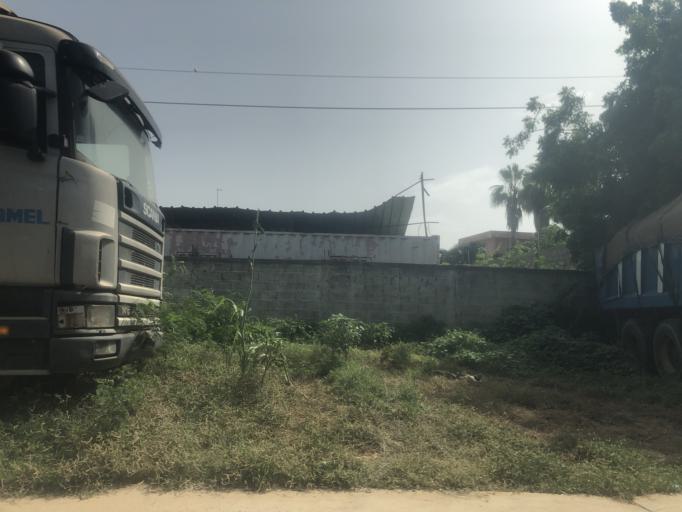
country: SN
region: Dakar
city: Mermoz Boabab
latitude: 14.7375
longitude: -17.5113
